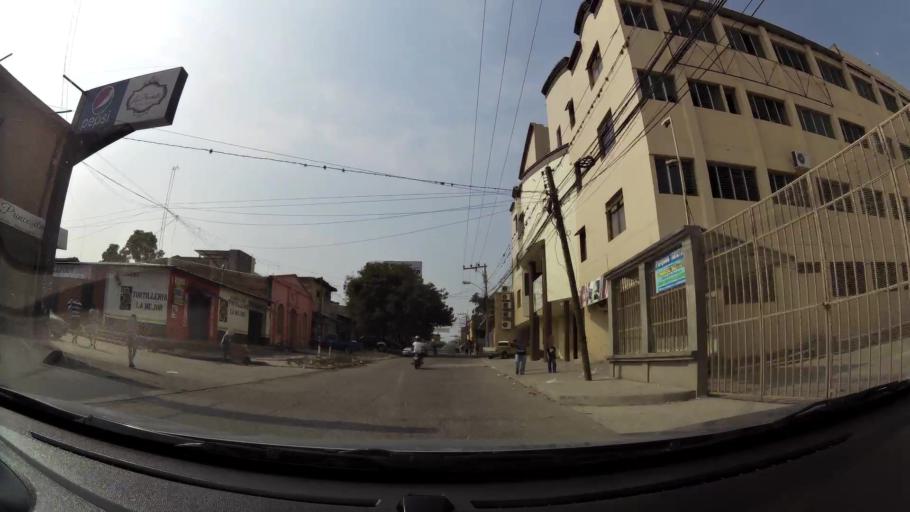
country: HN
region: Comayagua
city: Comayagua
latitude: 14.4540
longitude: -87.6390
